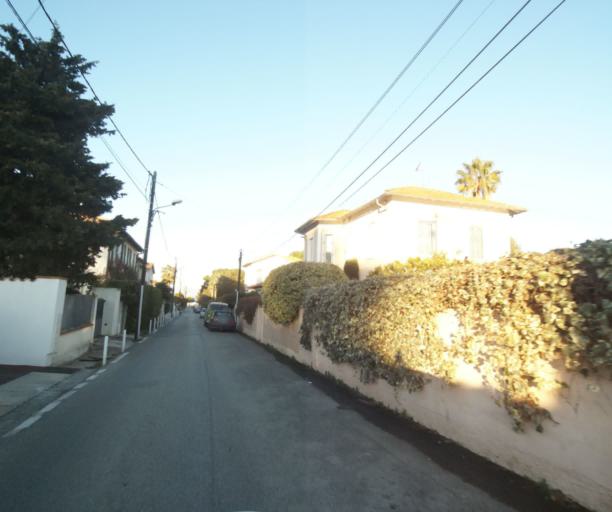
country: FR
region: Provence-Alpes-Cote d'Azur
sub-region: Departement des Alpes-Maritimes
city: Antibes
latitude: 43.5670
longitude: 7.1287
